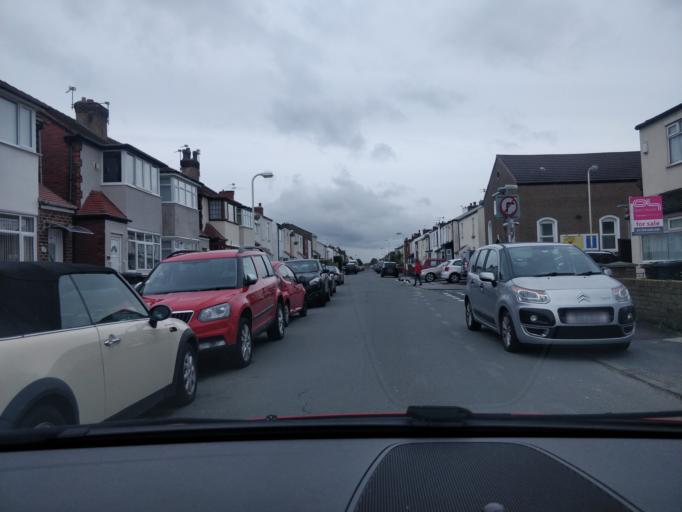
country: GB
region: England
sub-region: Sefton
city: Southport
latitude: 53.6377
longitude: -3.0072
